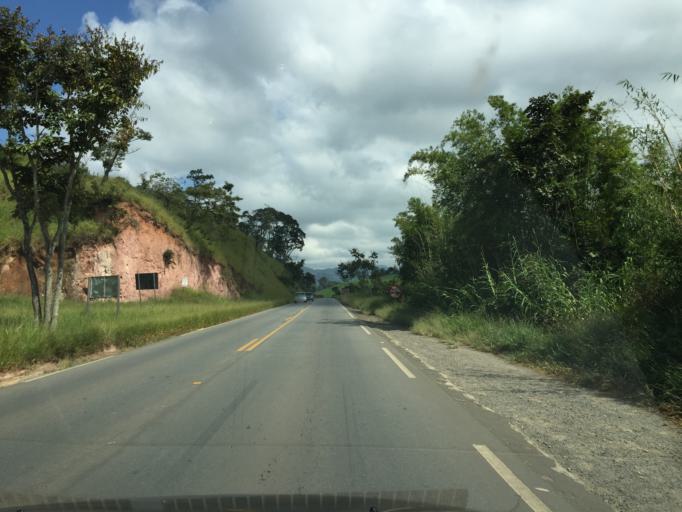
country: BR
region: Minas Gerais
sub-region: Passa Quatro
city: Passa Quatro
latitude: -22.3675
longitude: -44.9582
